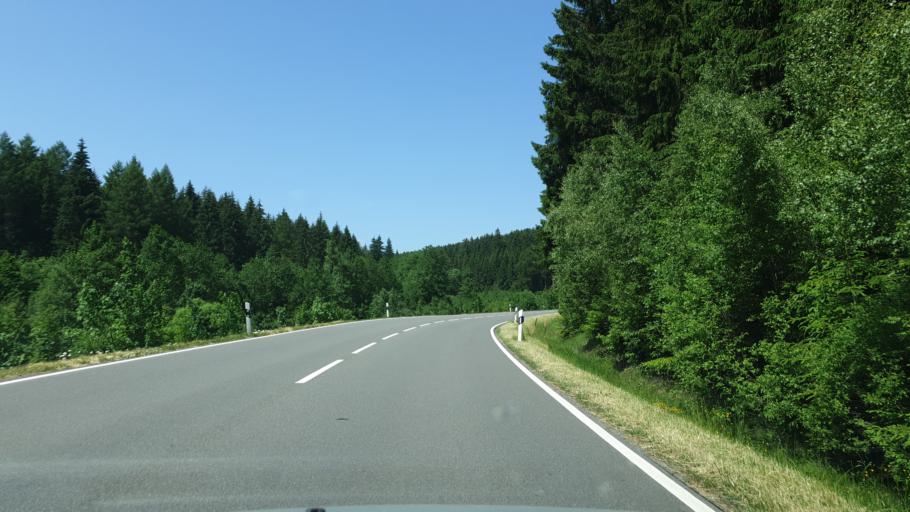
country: DE
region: Saxony
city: Zwota
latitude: 50.3896
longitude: 12.4355
